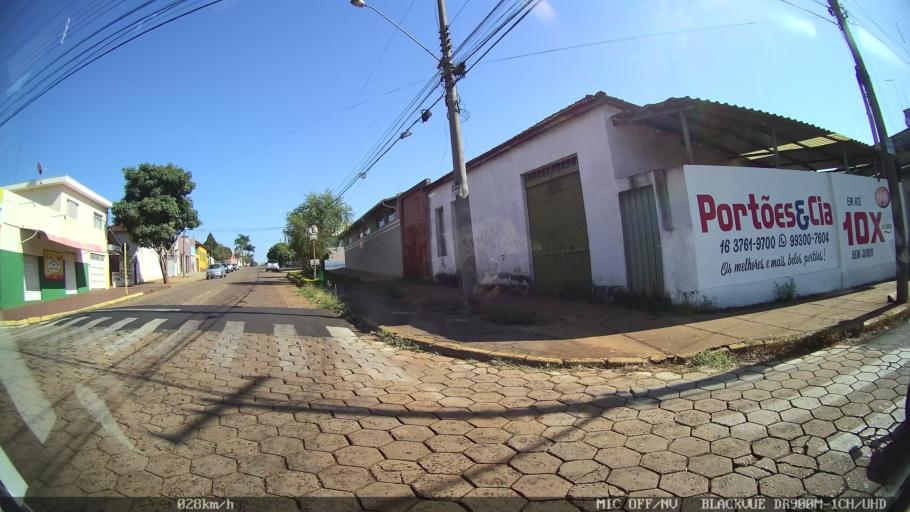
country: BR
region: Sao Paulo
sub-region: Batatais
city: Batatais
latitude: -20.8936
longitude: -47.5809
